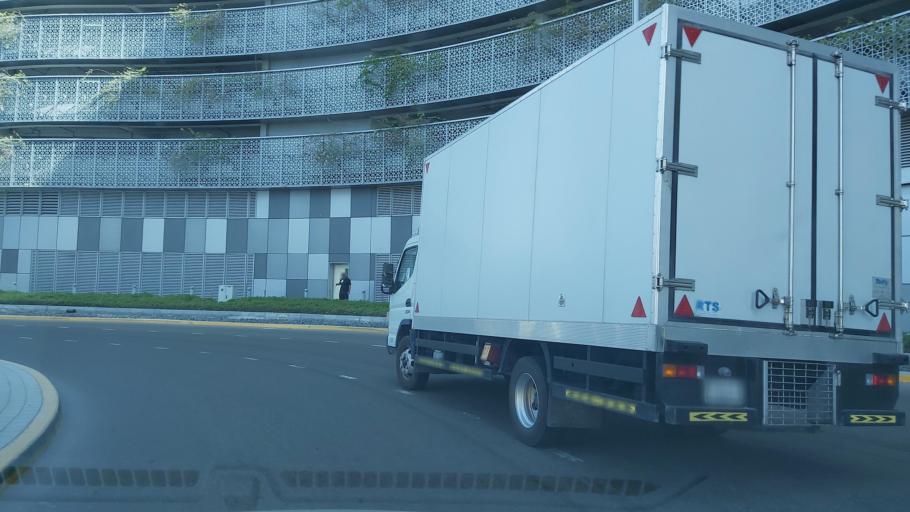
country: AE
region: Abu Dhabi
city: Abu Dhabi
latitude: 24.4985
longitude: 54.4047
